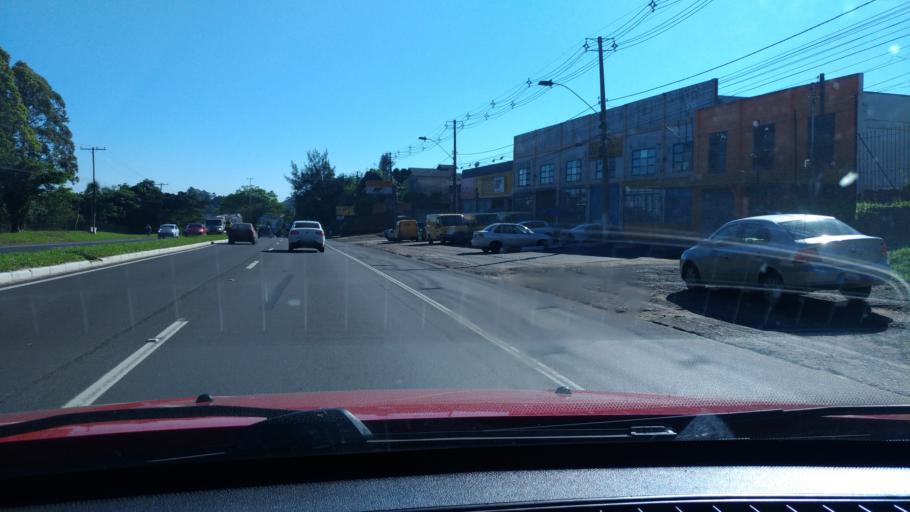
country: BR
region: Rio Grande do Sul
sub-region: Viamao
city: Viamao
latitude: -30.0843
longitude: -51.0549
